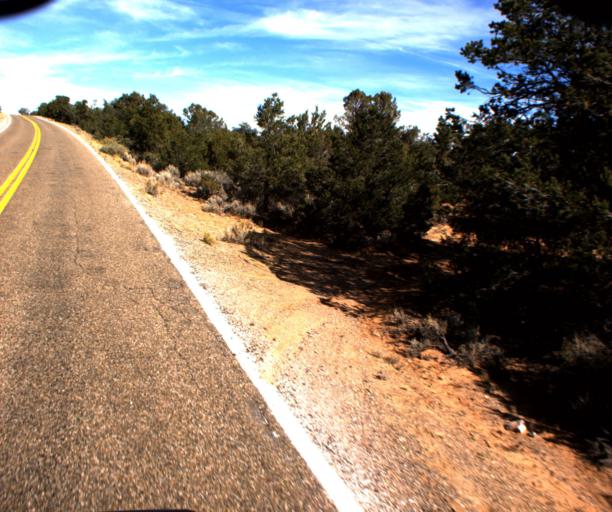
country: US
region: Arizona
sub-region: Navajo County
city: Kayenta
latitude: 36.6306
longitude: -110.5091
